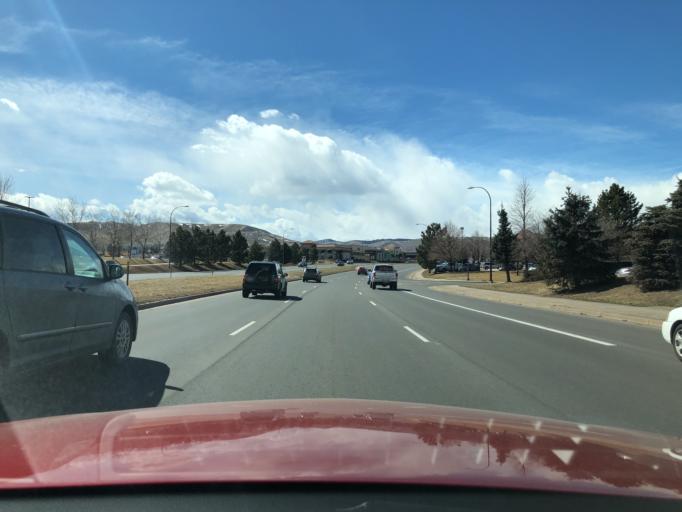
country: US
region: Colorado
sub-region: Jefferson County
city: West Pleasant View
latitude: 39.7342
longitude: -105.1609
